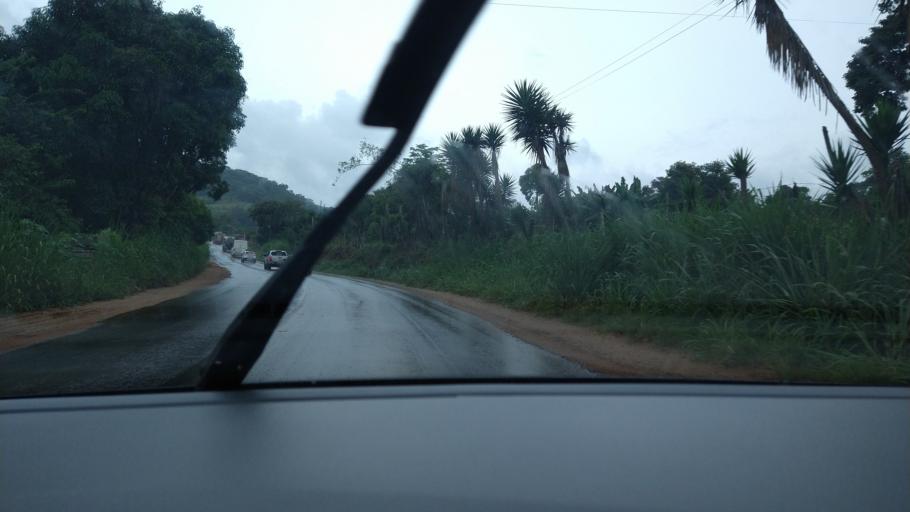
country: BR
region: Minas Gerais
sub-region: Vicosa
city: Vicosa
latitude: -20.6309
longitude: -42.8695
